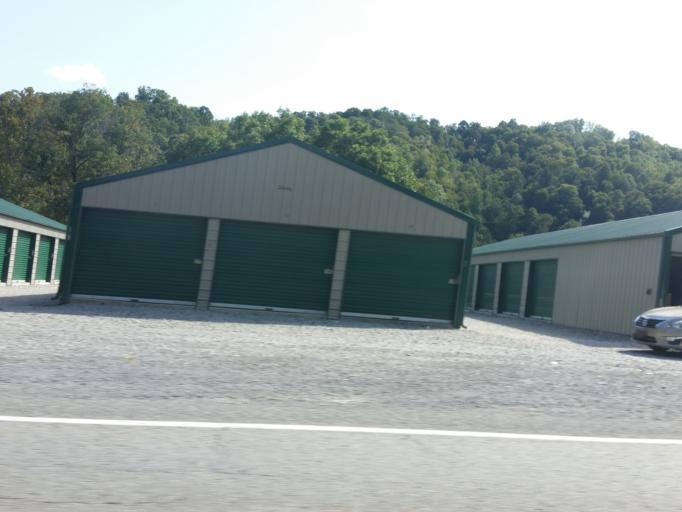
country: US
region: Kentucky
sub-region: Bell County
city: Pineville
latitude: 36.7300
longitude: -83.6568
